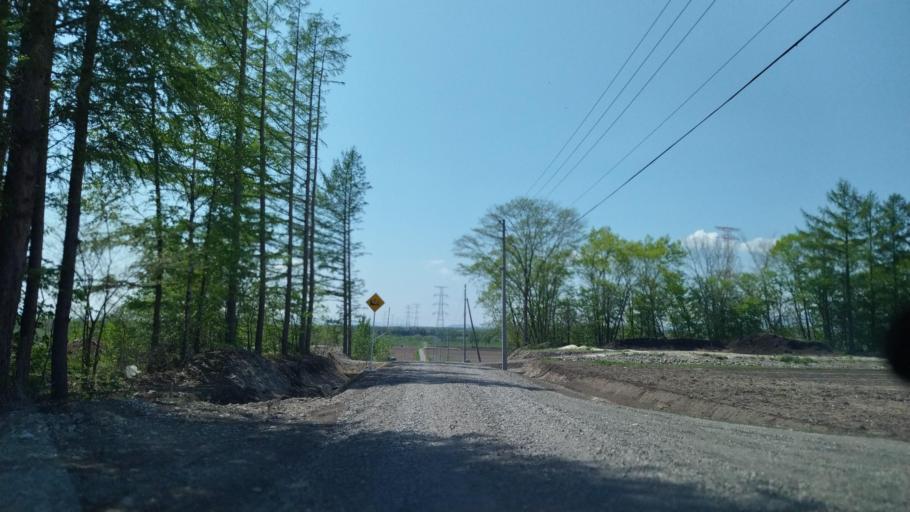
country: JP
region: Hokkaido
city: Otofuke
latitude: 43.1414
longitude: 143.2246
